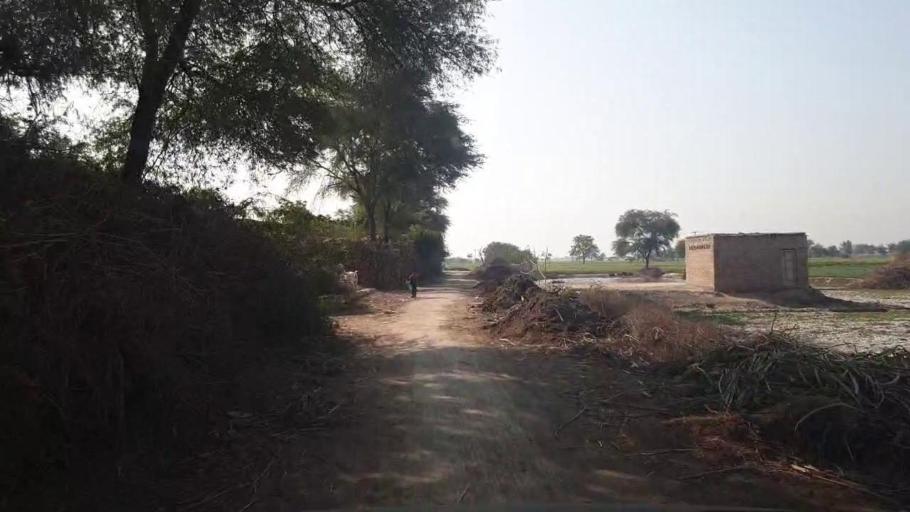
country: PK
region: Sindh
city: Bhit Shah
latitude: 25.7454
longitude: 68.5608
